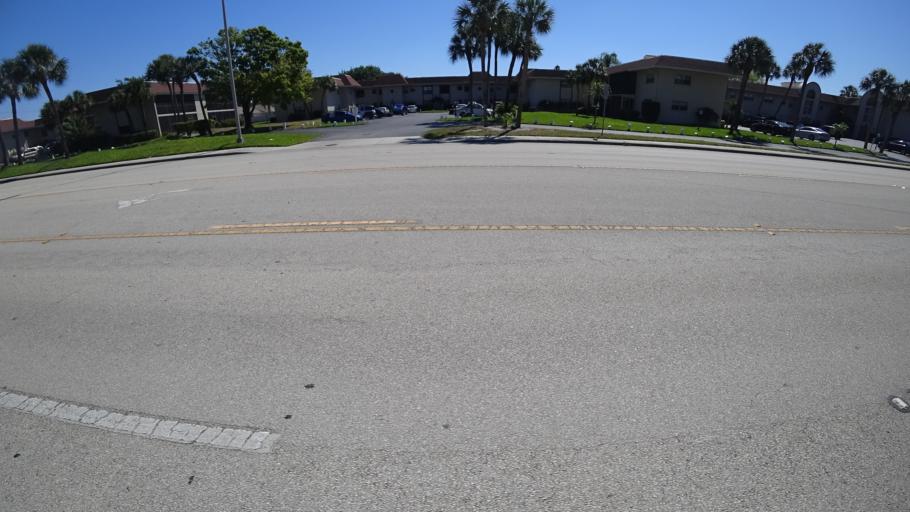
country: US
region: Florida
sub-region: Manatee County
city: West Bradenton
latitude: 27.4769
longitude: -82.6369
